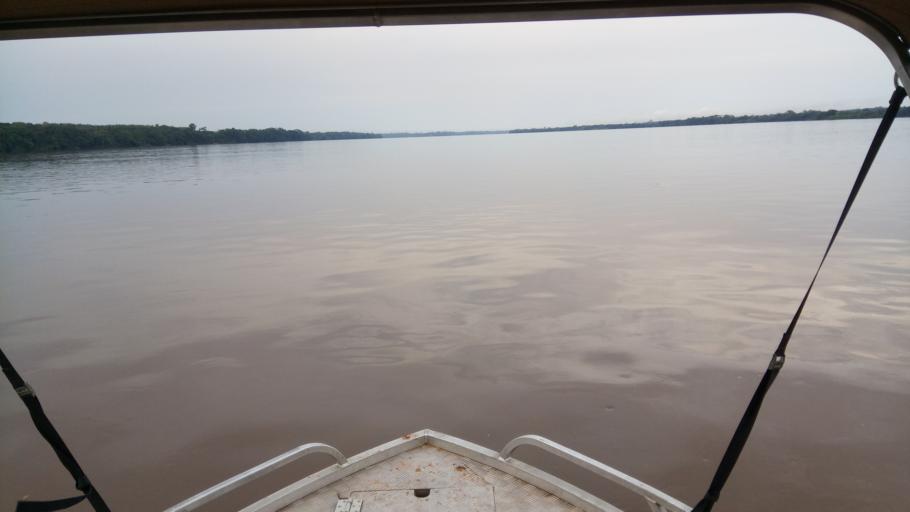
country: CD
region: Eastern Province
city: Kisangani
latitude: 0.5744
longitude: 24.8315
